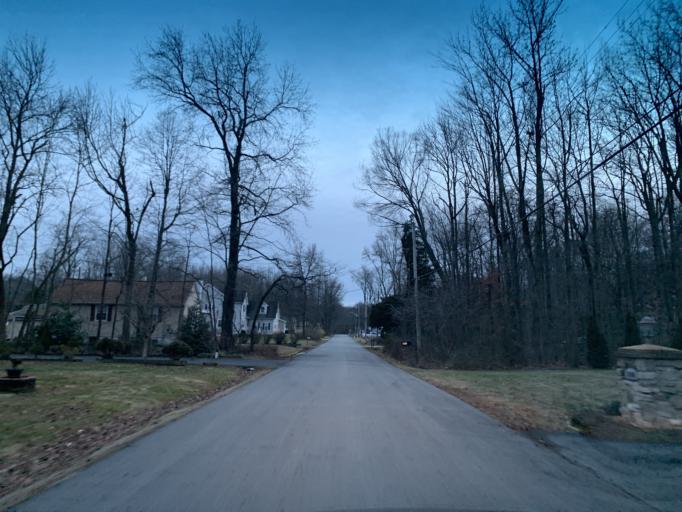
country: US
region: Maryland
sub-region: Baltimore County
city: Edgemere
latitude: 39.2801
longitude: -76.4187
